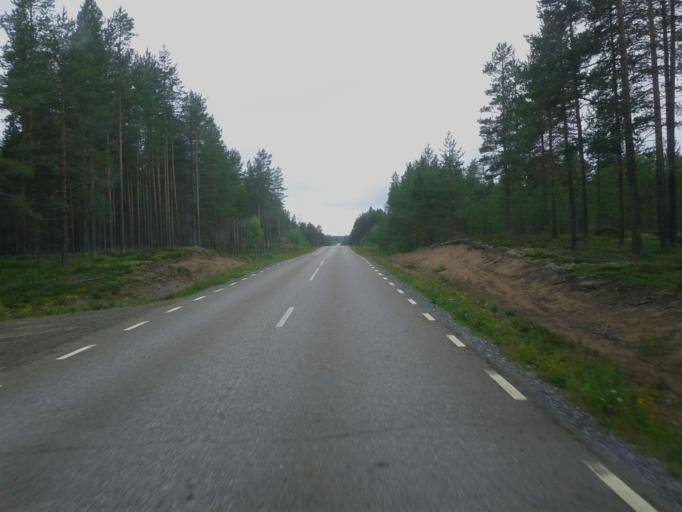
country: SE
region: Vaesterbotten
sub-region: Skelleftea Kommun
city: Kage
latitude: 64.9191
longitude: 20.9396
